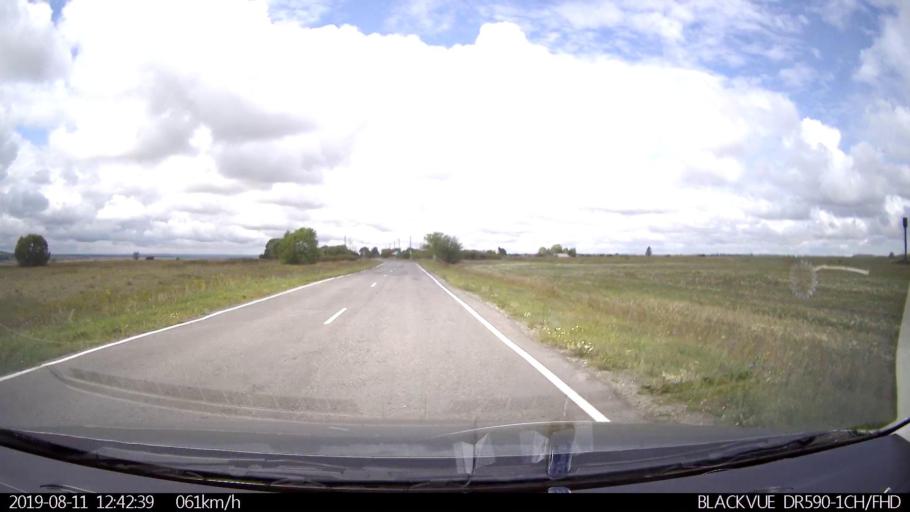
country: RU
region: Ulyanovsk
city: Ignatovka
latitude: 53.8474
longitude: 47.7490
